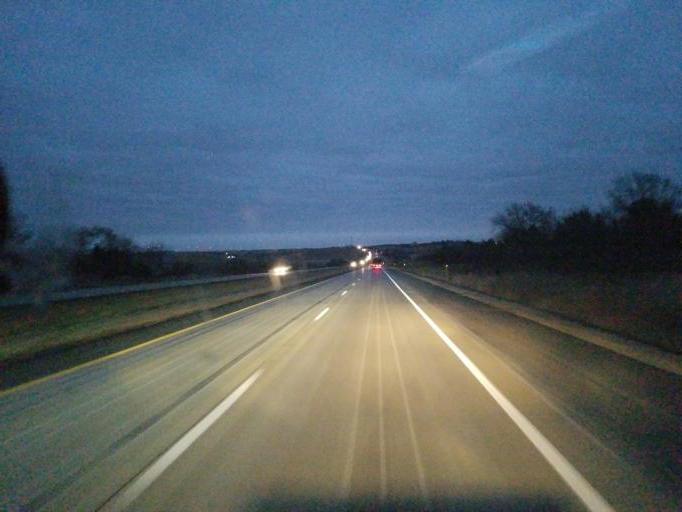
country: US
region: Iowa
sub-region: Cass County
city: Atlantic
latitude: 41.4968
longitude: -94.8082
